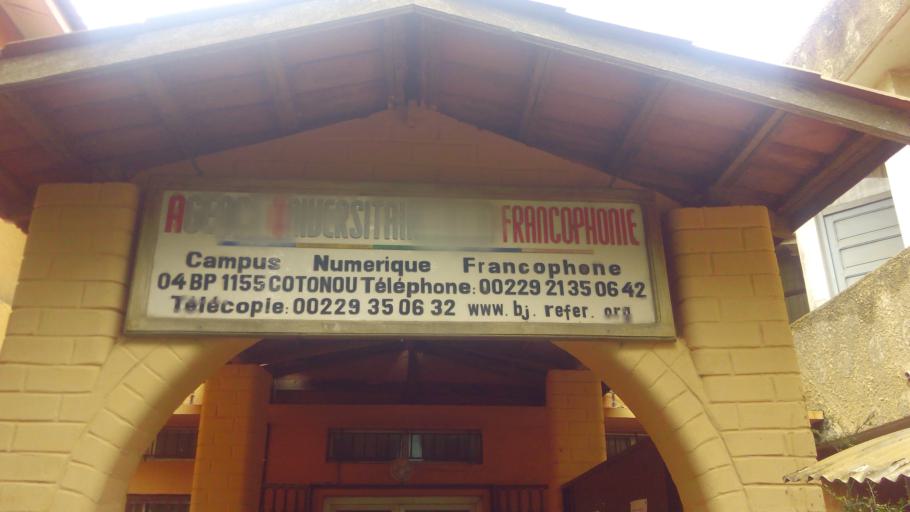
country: BJ
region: Atlantique
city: Abomey-Calavi
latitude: 6.4145
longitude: 2.3430
